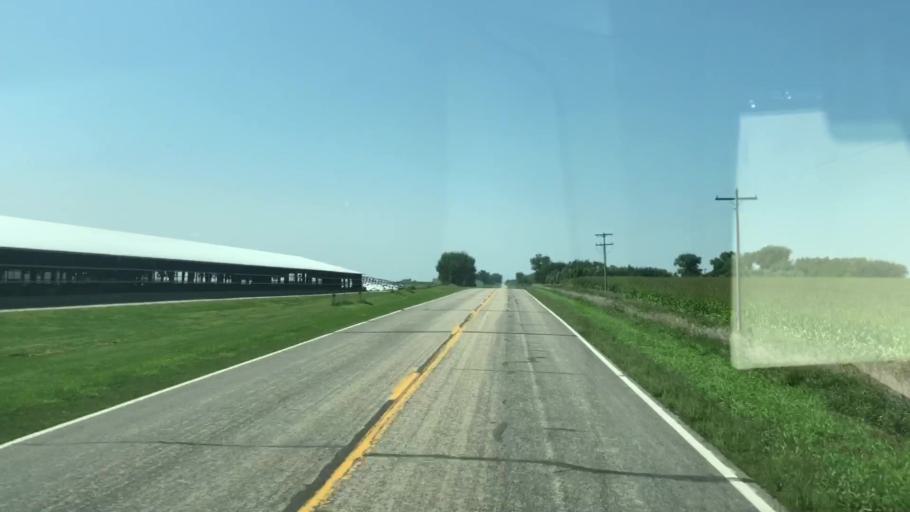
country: US
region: Iowa
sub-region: O'Brien County
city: Sanborn
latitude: 43.2728
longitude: -95.6961
